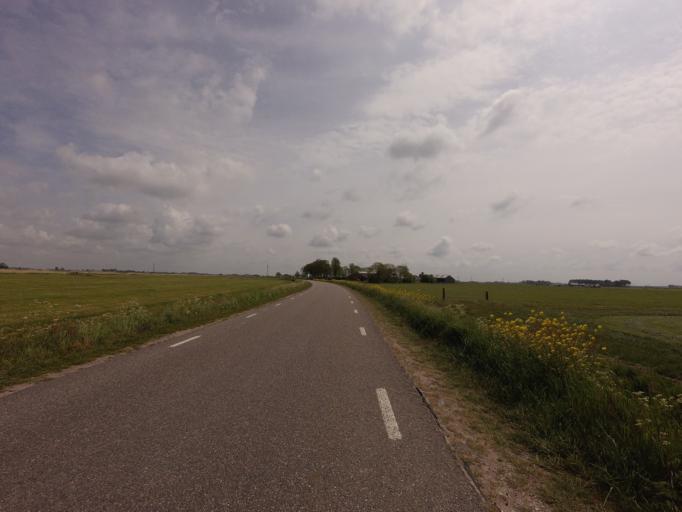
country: NL
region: Friesland
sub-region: Sudwest Fryslan
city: Bolsward
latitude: 53.1082
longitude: 5.4935
